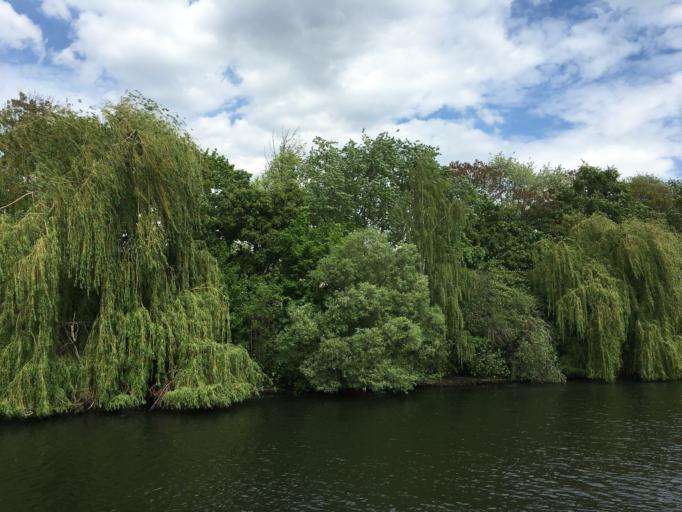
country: DE
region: Berlin
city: Hansaviertel
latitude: 52.5177
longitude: 13.3303
